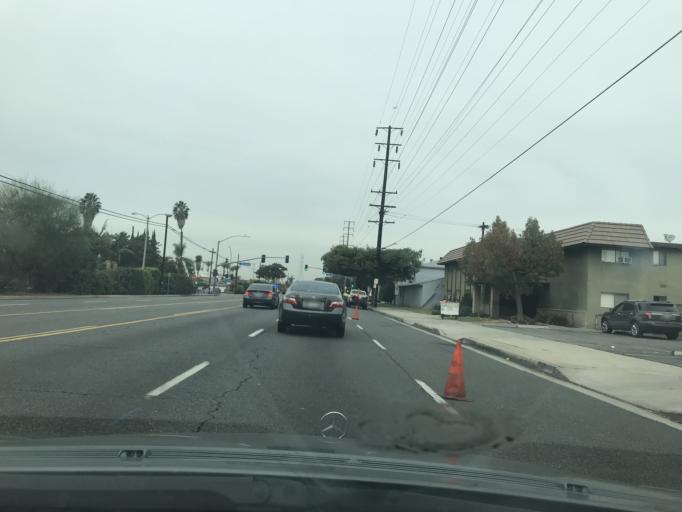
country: US
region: California
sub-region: Los Angeles County
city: Downey
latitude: 33.9568
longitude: -118.1362
